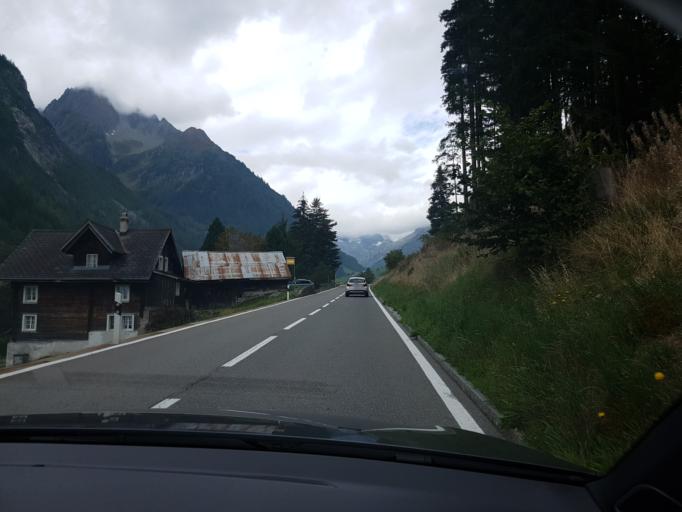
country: CH
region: Uri
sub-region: Uri
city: Andermatt
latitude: 46.7183
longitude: 8.5744
